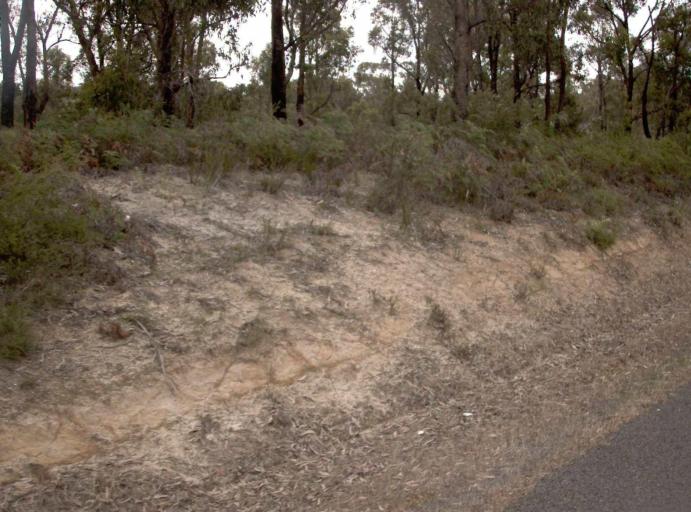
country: AU
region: Victoria
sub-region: Wellington
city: Sale
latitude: -38.3297
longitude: 147.0179
